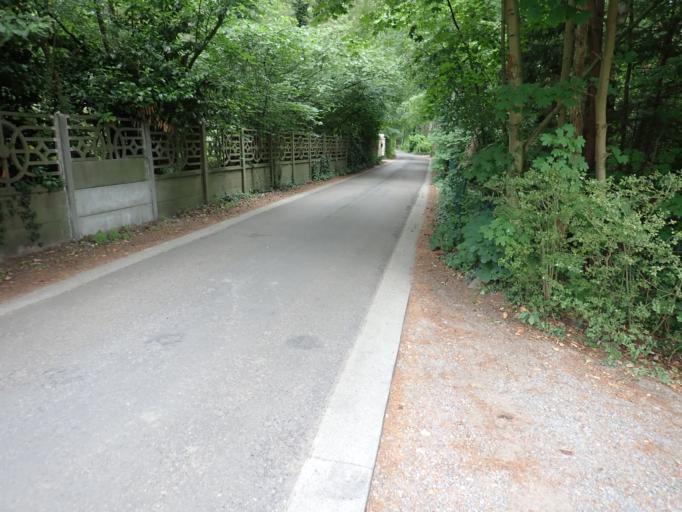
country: BE
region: Flanders
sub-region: Provincie Vlaams-Brabant
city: Keerbergen
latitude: 51.0080
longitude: 4.6007
